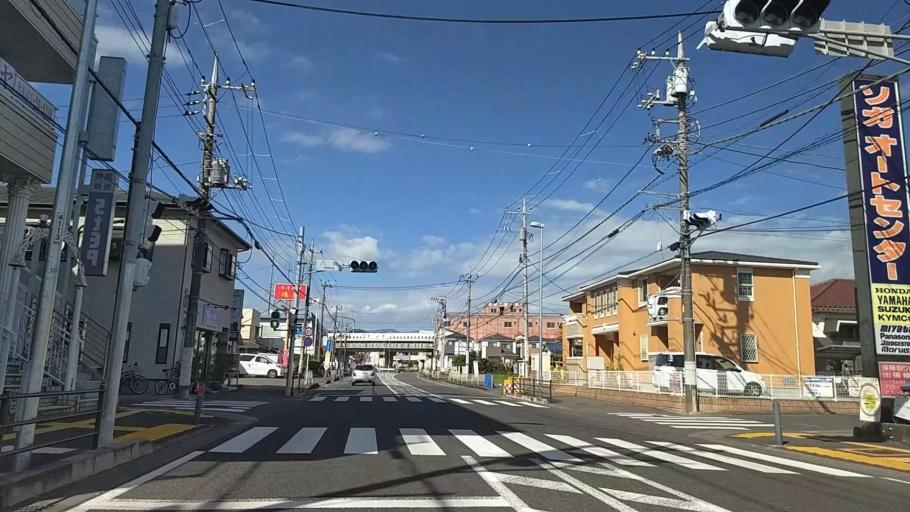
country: JP
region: Kanagawa
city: Ninomiya
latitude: 35.3072
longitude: 139.2531
